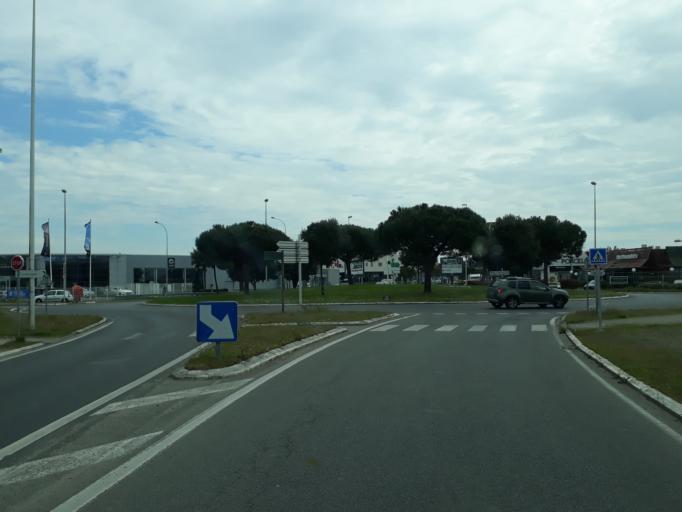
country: FR
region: Pays de la Loire
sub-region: Departement de la Loire-Atlantique
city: La Baule-Escoublac
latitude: 47.2947
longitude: -2.3987
